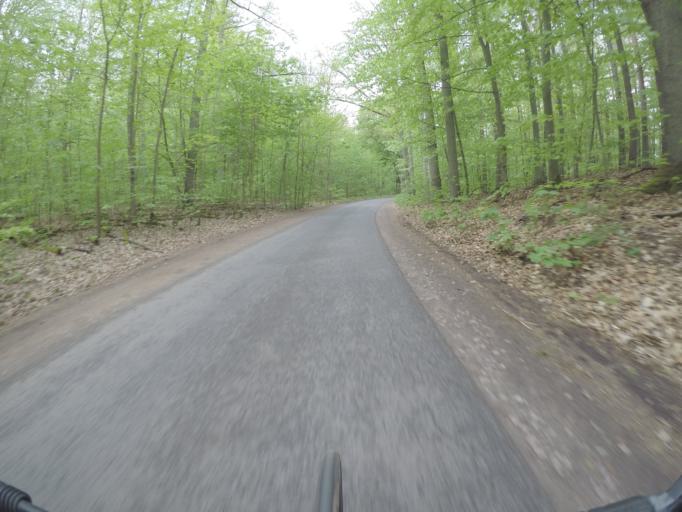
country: DE
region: Brandenburg
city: Marienwerder
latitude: 52.8913
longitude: 13.6441
